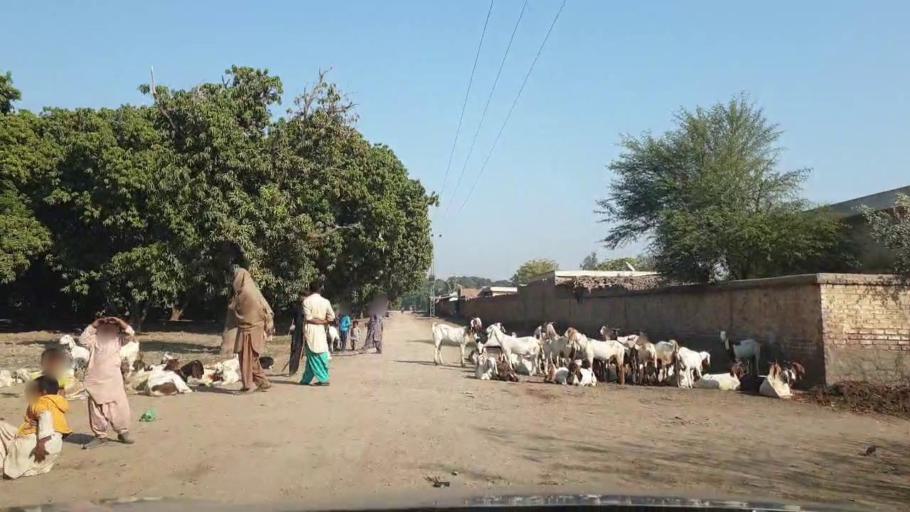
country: PK
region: Sindh
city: Tando Allahyar
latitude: 25.5135
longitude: 68.7190
